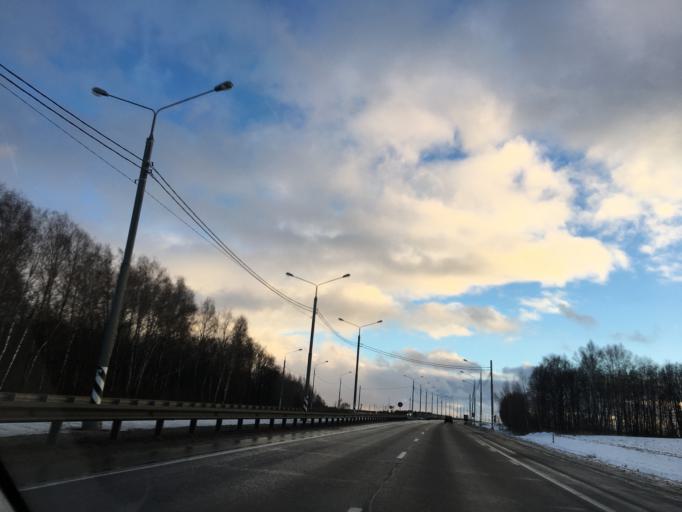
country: RU
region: Tula
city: Zaokskiy
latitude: 54.8131
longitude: 37.4806
